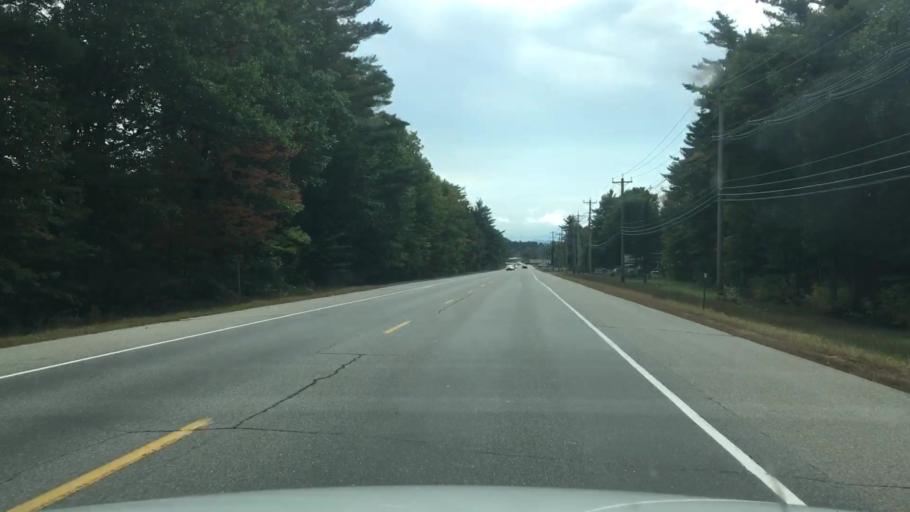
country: US
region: New Hampshire
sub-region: Carroll County
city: North Conway
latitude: 44.0949
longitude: -71.1503
